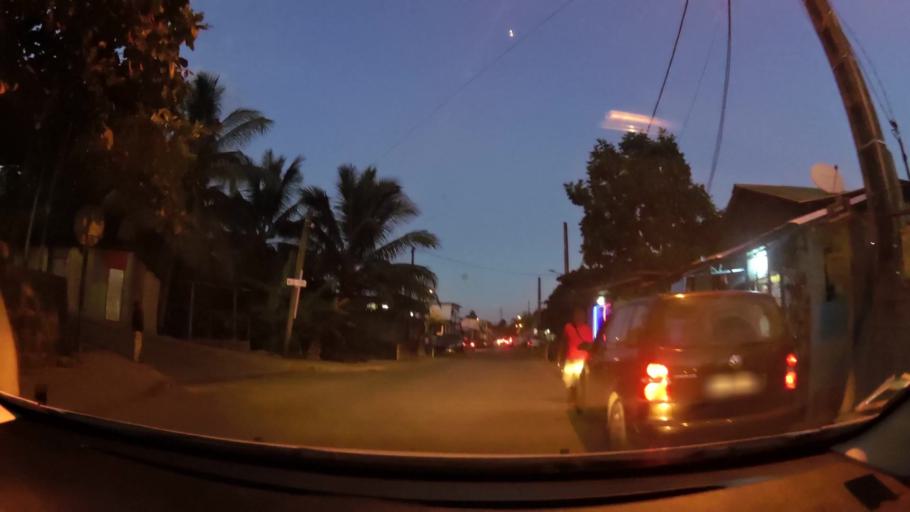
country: YT
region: Bandraboua
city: Bandraboua
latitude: -12.7225
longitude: 45.1189
